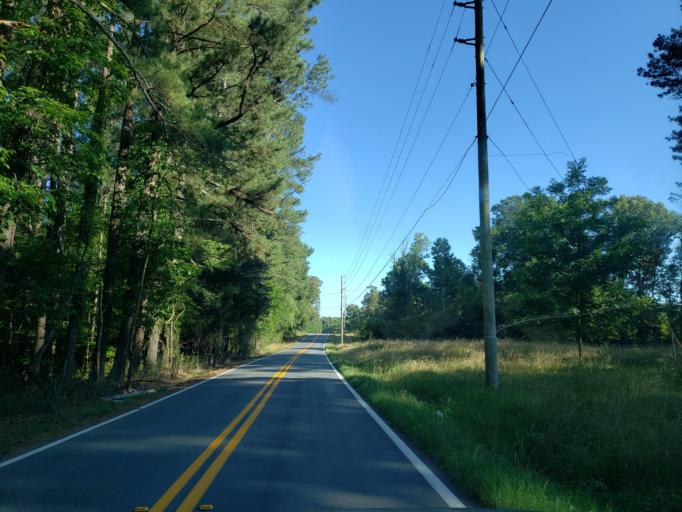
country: US
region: Georgia
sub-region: Floyd County
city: Shannon
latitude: 34.4705
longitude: -85.1170
